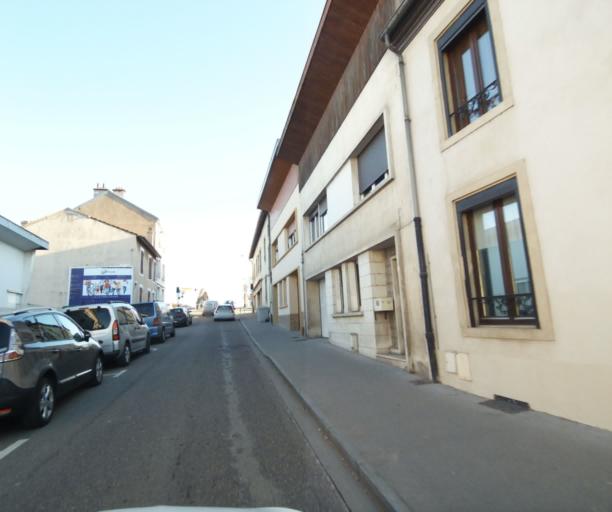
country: FR
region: Lorraine
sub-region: Departement de Meurthe-et-Moselle
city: Maxeville
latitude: 48.7048
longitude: 6.1742
